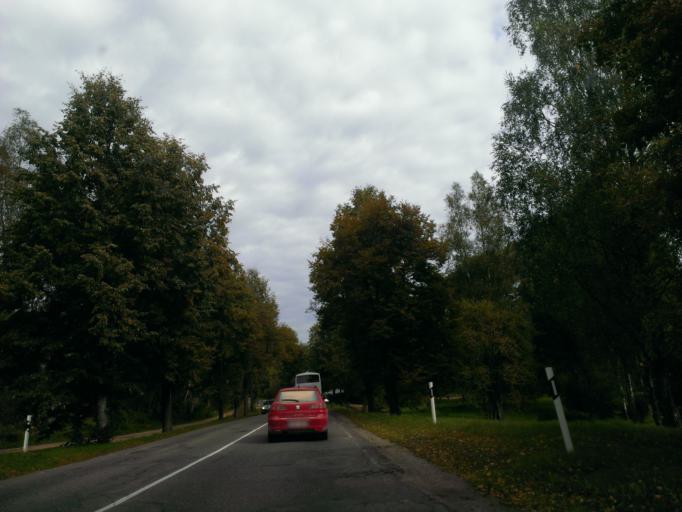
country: LV
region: Sigulda
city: Sigulda
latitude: 57.1762
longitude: 24.8460
